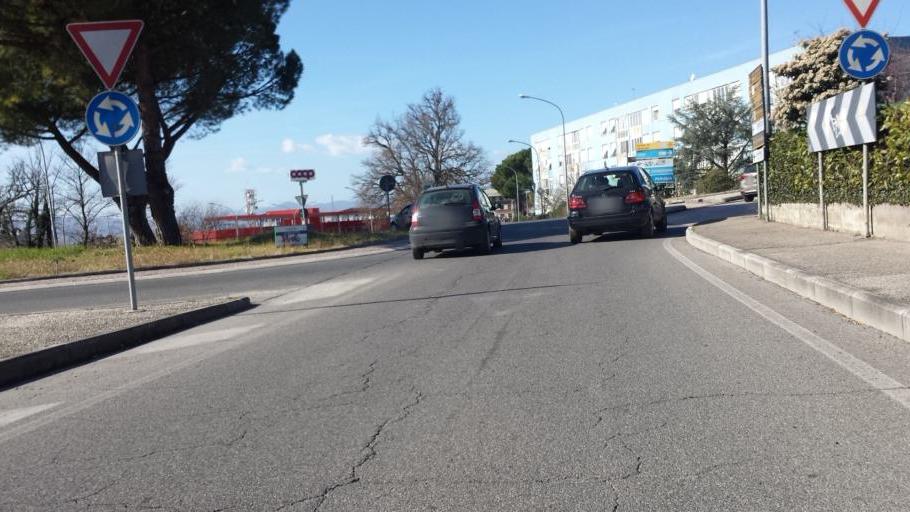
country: IT
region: Umbria
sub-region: Provincia di Terni
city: Terni
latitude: 42.5881
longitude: 12.6055
